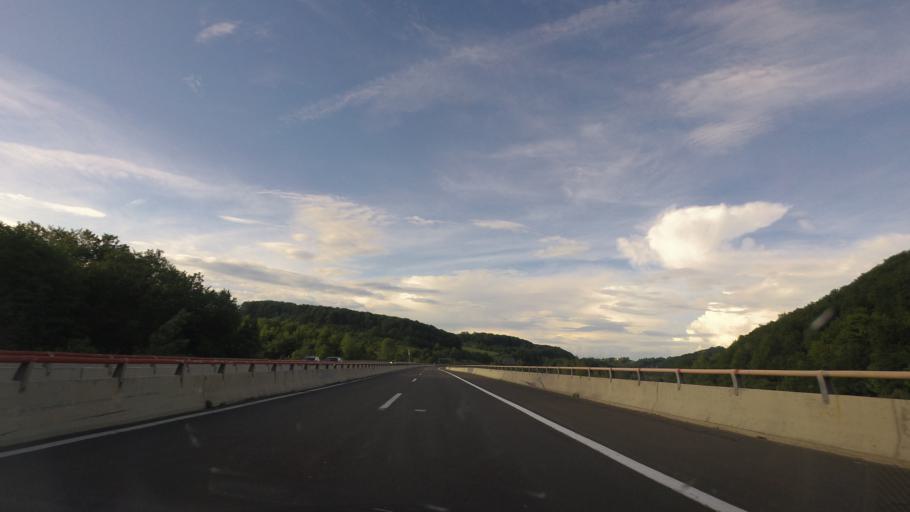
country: HR
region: Karlovacka
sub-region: Grad Karlovac
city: Karlovac
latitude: 45.4932
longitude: 15.4469
